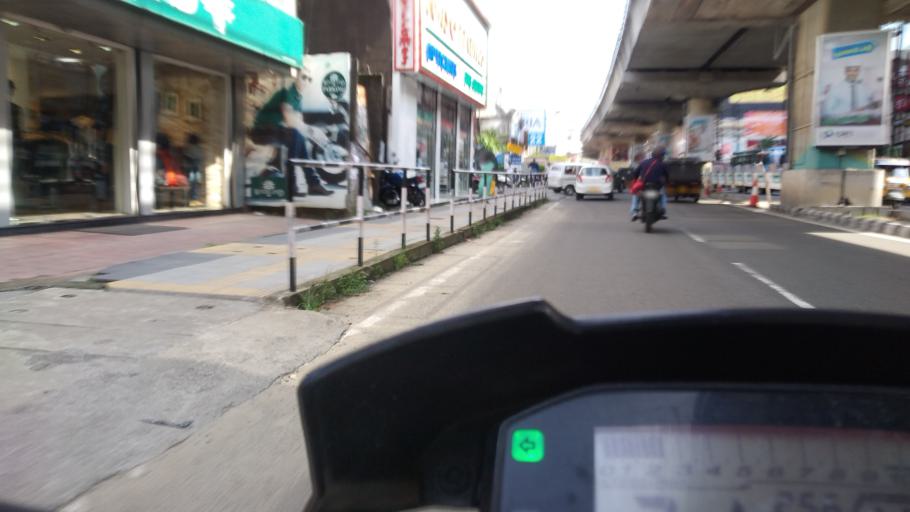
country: IN
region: Kerala
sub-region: Ernakulam
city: Cochin
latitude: 9.9791
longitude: 76.2834
